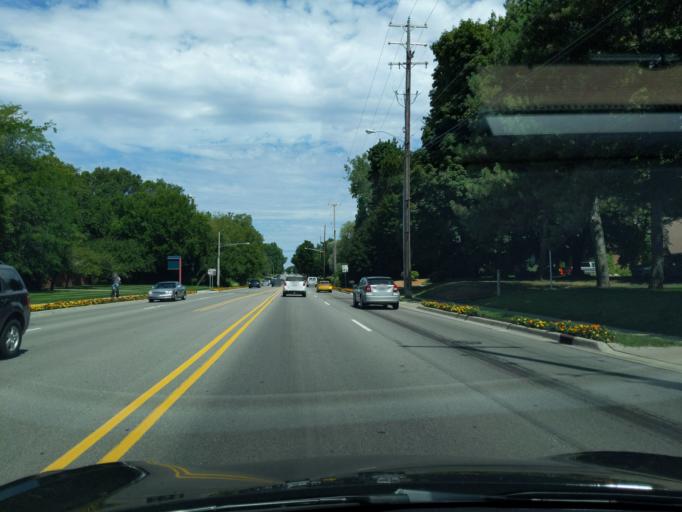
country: US
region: Michigan
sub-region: Midland County
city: Midland
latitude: 43.6257
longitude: -84.2470
